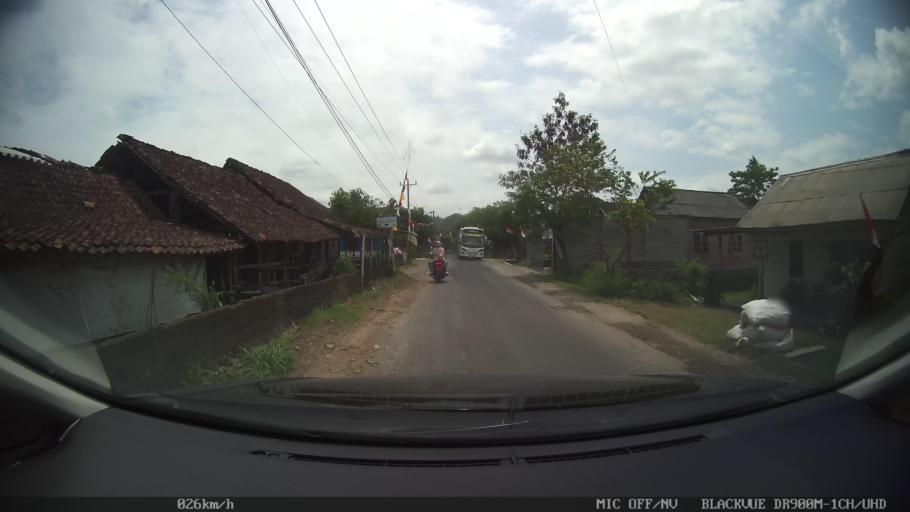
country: ID
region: Central Java
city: Candi Prambanan
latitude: -7.7827
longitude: 110.4893
